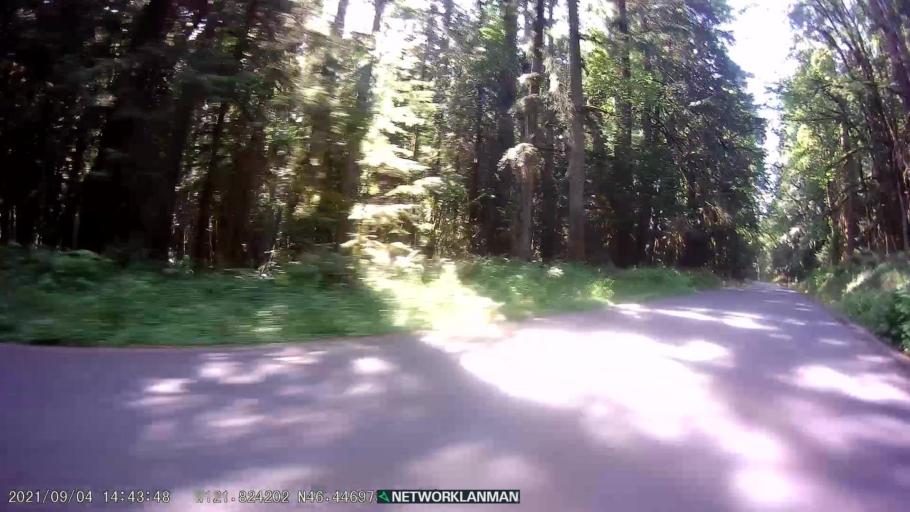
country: US
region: Washington
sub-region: Lewis County
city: Morton
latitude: 46.4474
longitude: -121.8239
